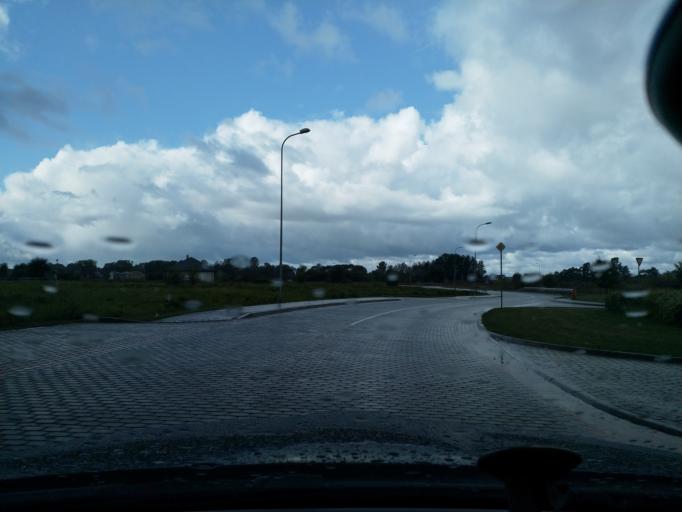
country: LV
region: Ventspils
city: Ventspils
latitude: 57.3710
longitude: 21.5863
